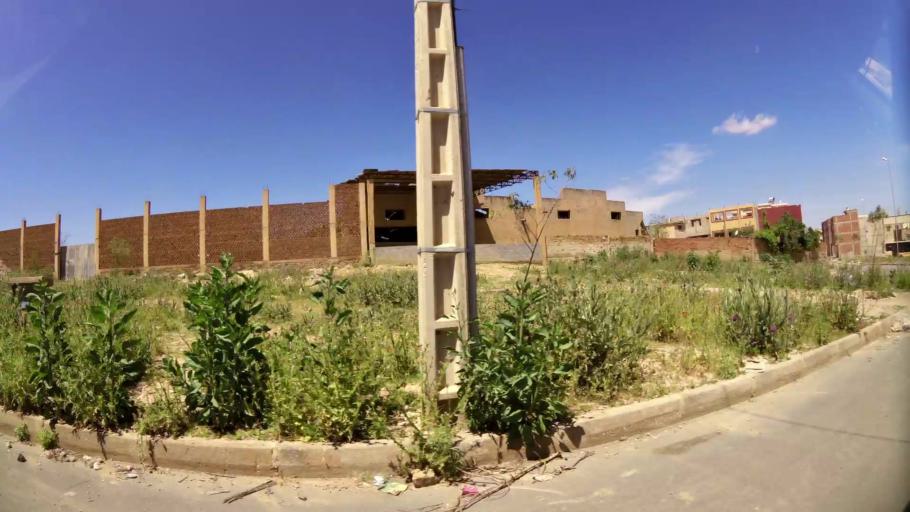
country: MA
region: Oriental
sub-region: Oujda-Angad
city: Oujda
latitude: 34.6590
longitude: -1.9461
